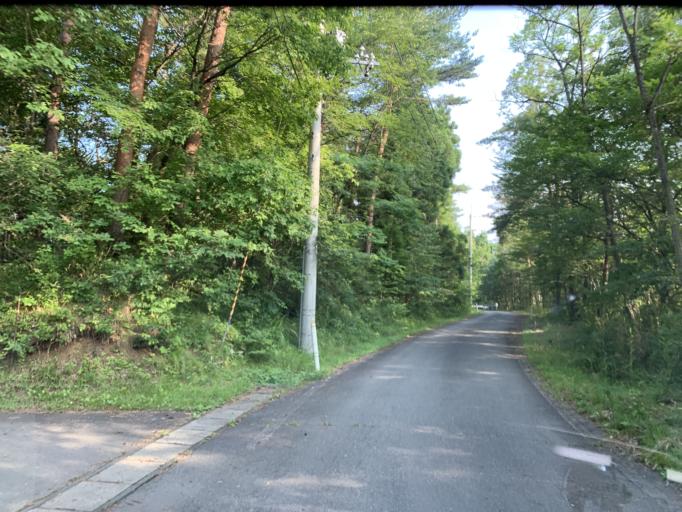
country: JP
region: Iwate
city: Ichinoseki
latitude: 38.8323
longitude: 141.1501
